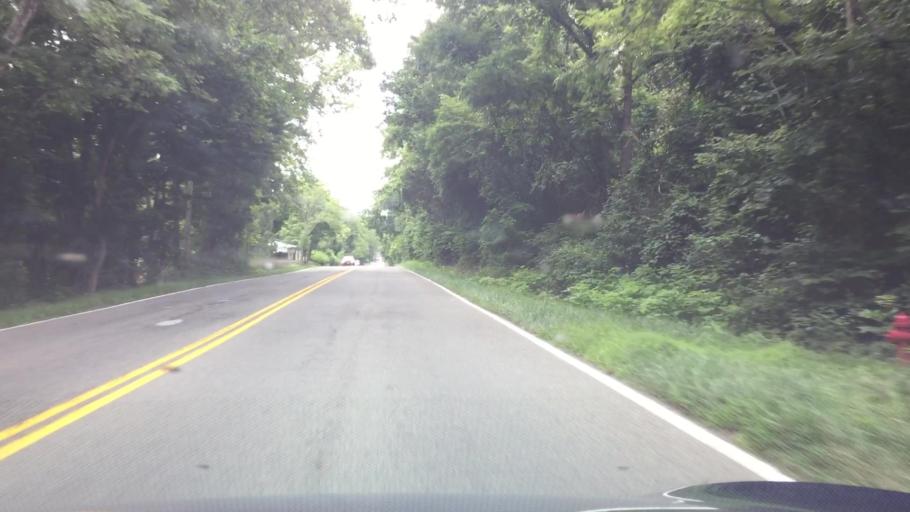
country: US
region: Virginia
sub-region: Pulaski County
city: Pulaski
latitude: 36.9499
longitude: -80.9080
